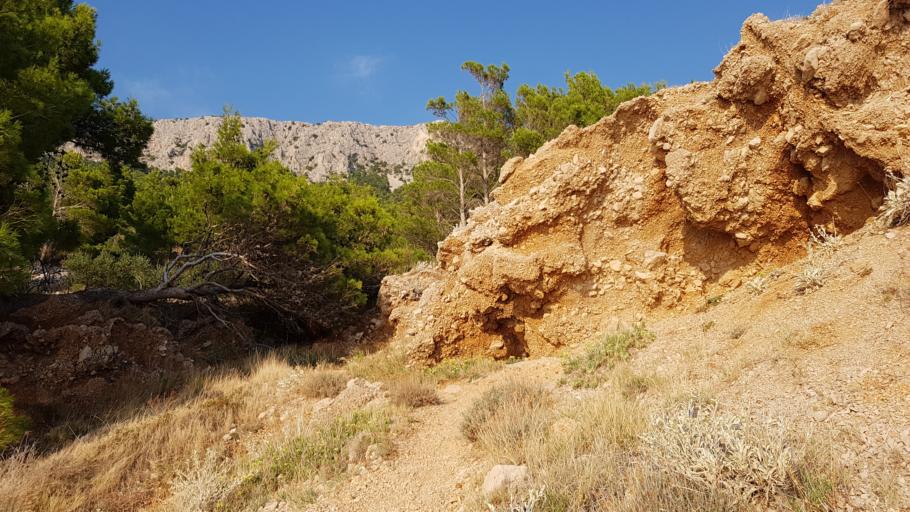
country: HR
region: Splitsko-Dalmatinska
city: Donja Brela
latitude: 43.3903
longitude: 16.8953
